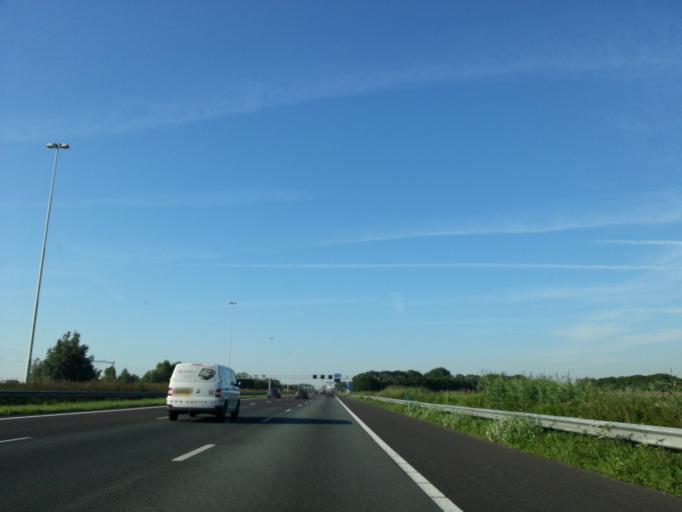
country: NL
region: South Holland
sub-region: Gemeente Dordrecht
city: Dordrecht
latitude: 51.7535
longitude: 4.6424
